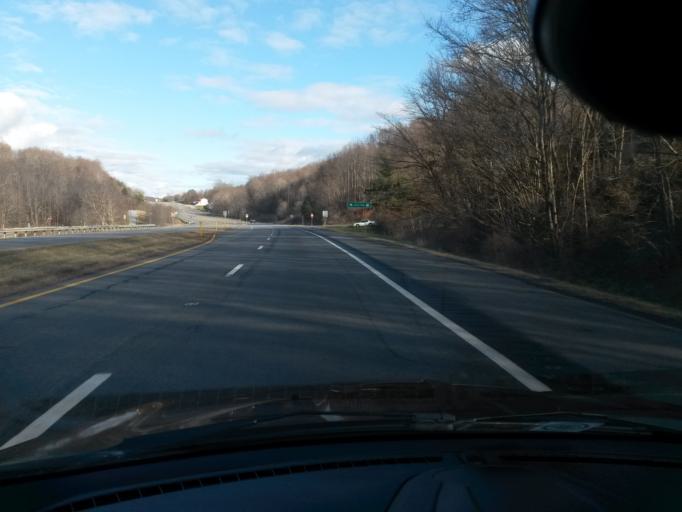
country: US
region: West Virginia
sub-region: Mercer County
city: Bluefield
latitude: 37.2762
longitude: -81.1488
